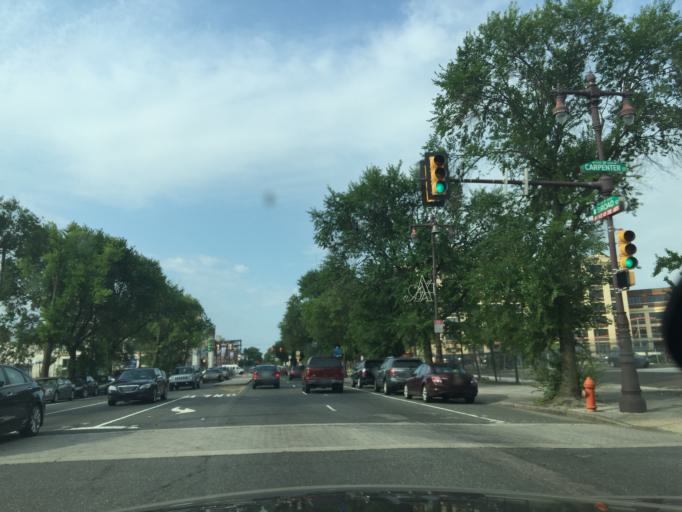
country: US
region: Pennsylvania
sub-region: Philadelphia County
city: Philadelphia
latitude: 39.9392
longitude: -75.1665
